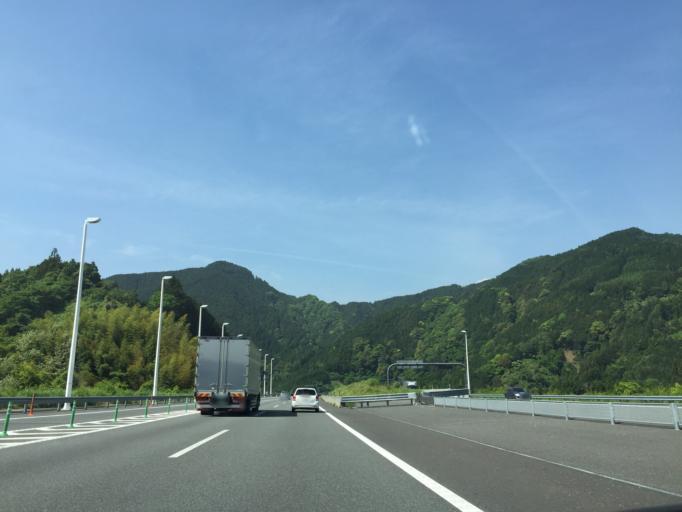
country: JP
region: Shizuoka
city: Fujinomiya
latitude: 35.1299
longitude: 138.5072
